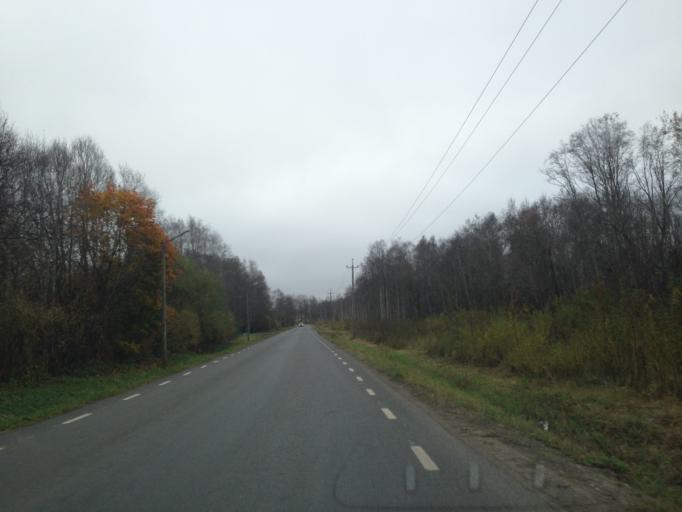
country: EE
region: Harju
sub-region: Harku vald
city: Tabasalu
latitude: 59.3769
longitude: 24.5390
